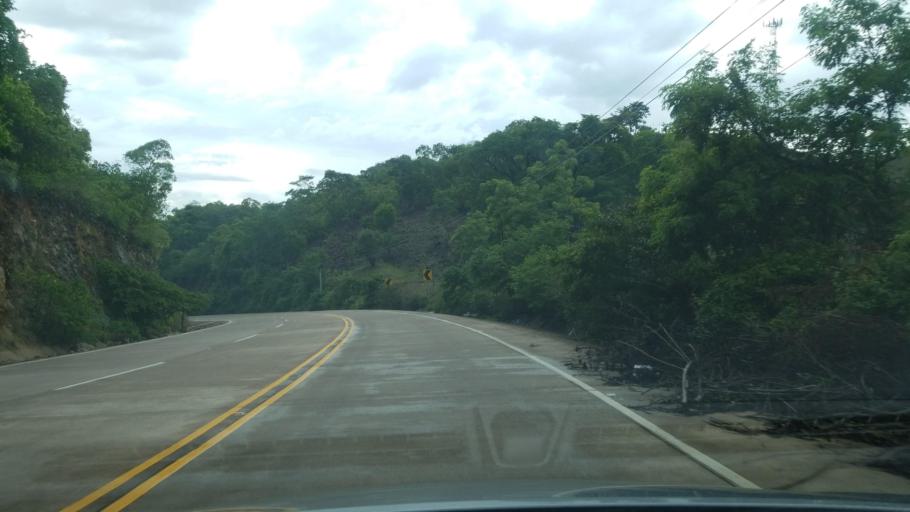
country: HN
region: Copan
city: Copan
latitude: 14.8566
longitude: -89.2088
